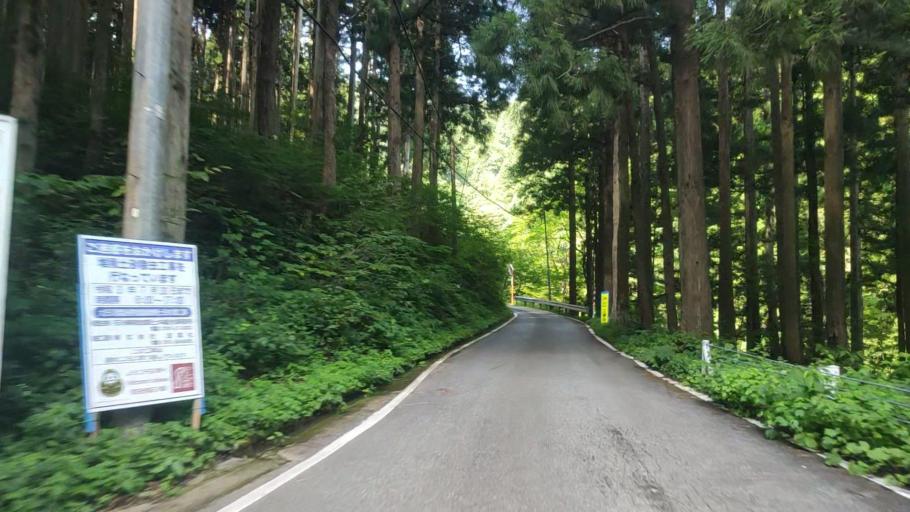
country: JP
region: Fukui
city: Katsuyama
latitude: 36.2289
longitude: 136.5314
